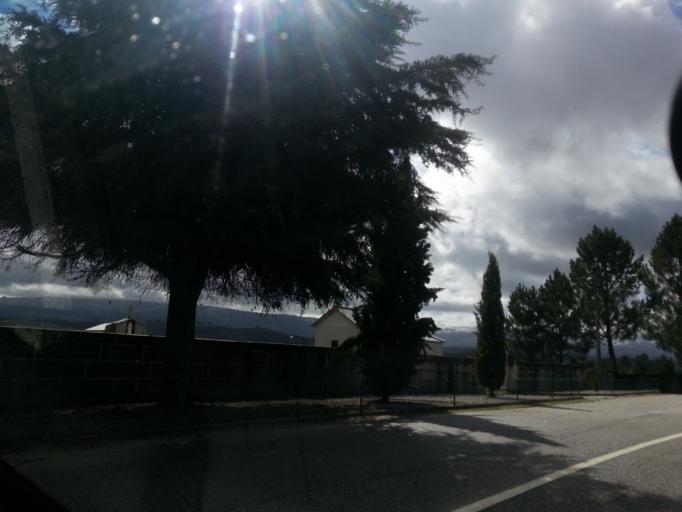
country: PT
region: Guarda
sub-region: Fornos de Algodres
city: Fornos de Algodres
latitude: 40.6129
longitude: -7.4857
